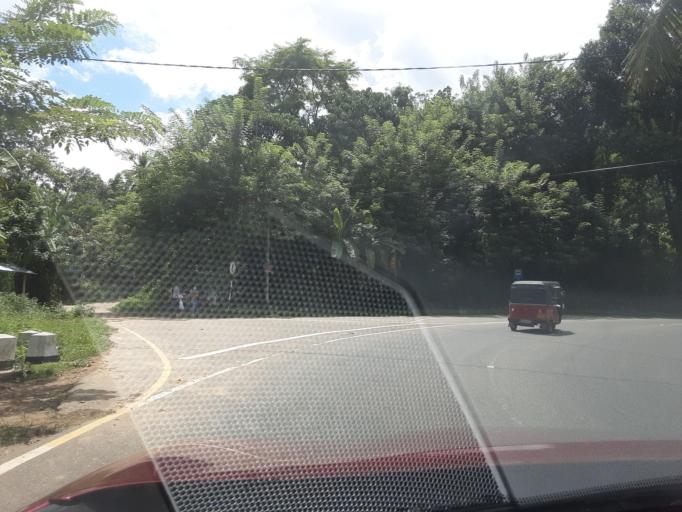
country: LK
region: Uva
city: Monaragala
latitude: 6.8948
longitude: 81.2536
